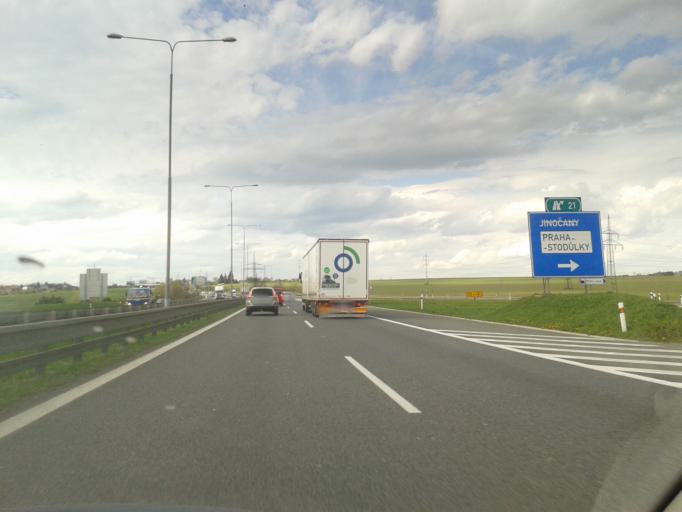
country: CZ
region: Central Bohemia
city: Rudna
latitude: 50.0302
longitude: 14.2850
